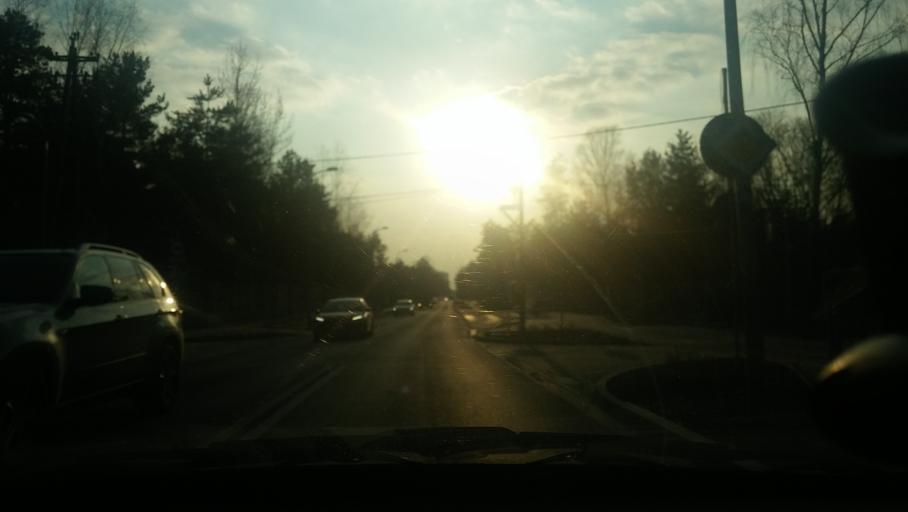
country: PL
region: Masovian Voivodeship
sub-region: Warszawa
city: Wawer
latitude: 52.2113
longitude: 21.2117
